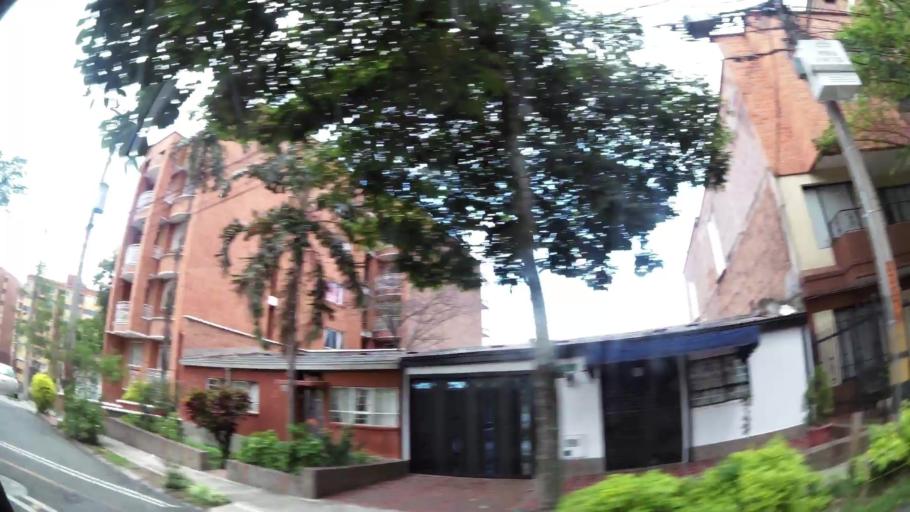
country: CO
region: Antioquia
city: Envigado
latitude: 6.1675
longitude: -75.5899
